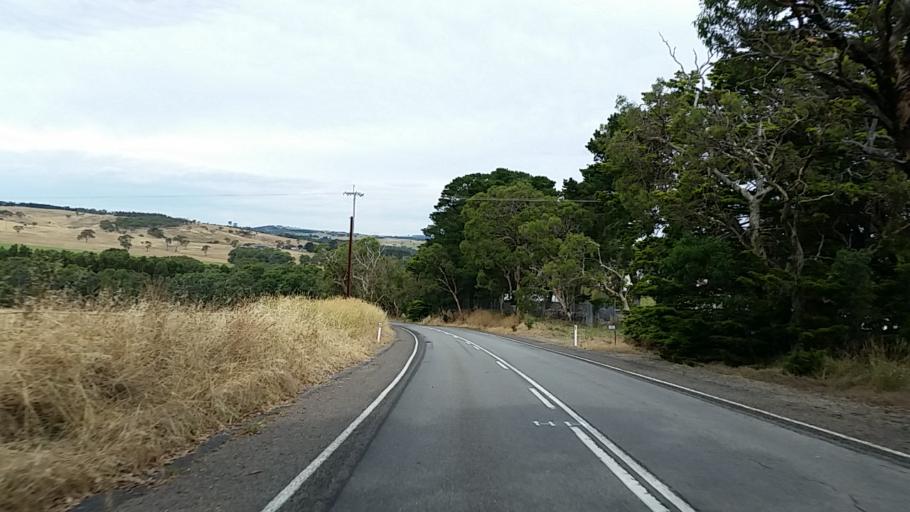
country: AU
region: South Australia
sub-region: Onkaparinga
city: Aldinga
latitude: -35.3773
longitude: 138.4618
